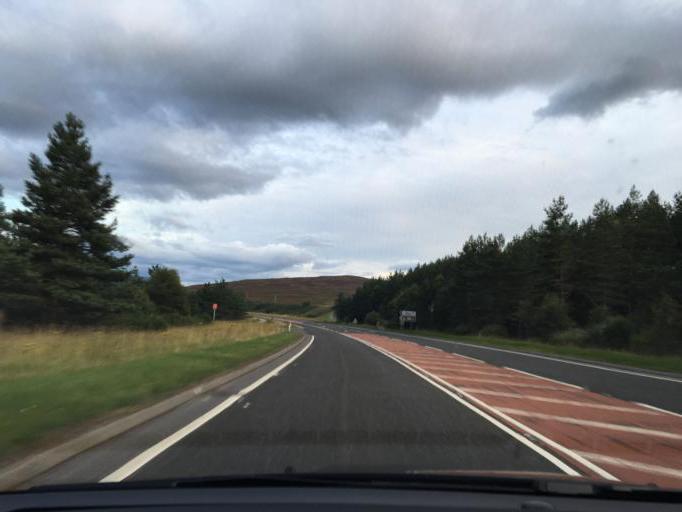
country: GB
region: Scotland
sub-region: Highland
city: Inverness
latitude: 57.3688
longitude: -4.0251
